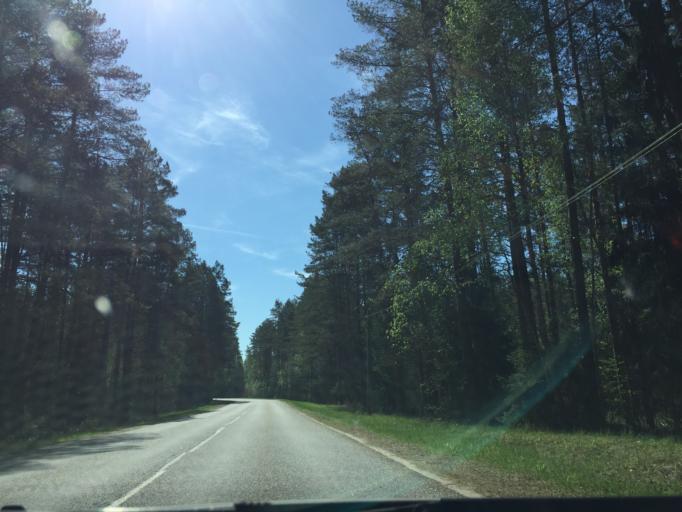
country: LV
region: Garkalne
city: Garkalne
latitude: 57.0174
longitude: 24.4417
